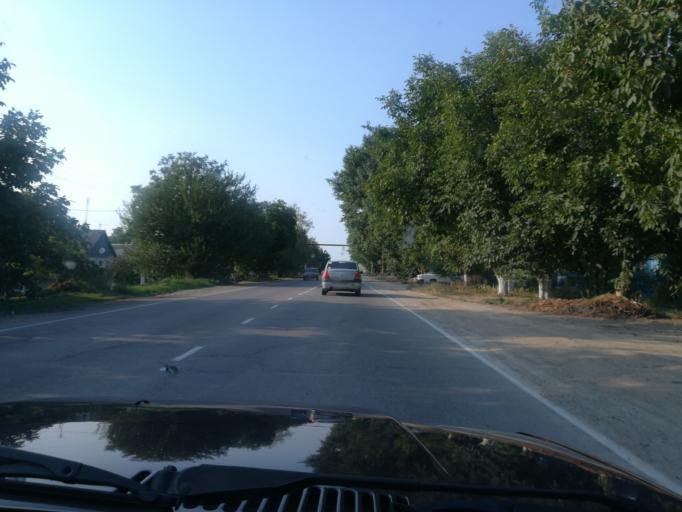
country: RU
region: Krasnodarskiy
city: Yurovka
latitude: 45.1161
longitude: 37.4220
